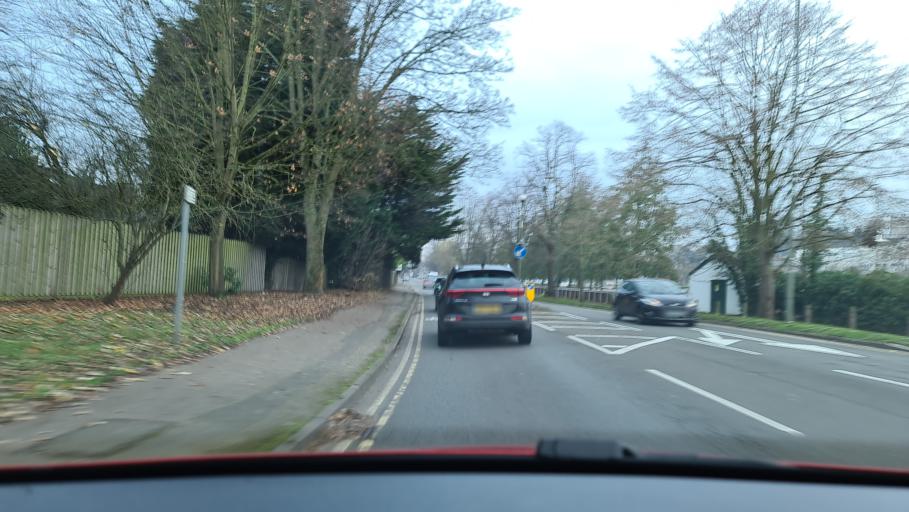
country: GB
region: England
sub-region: Surrey
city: Esher
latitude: 51.3742
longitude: -0.3585
